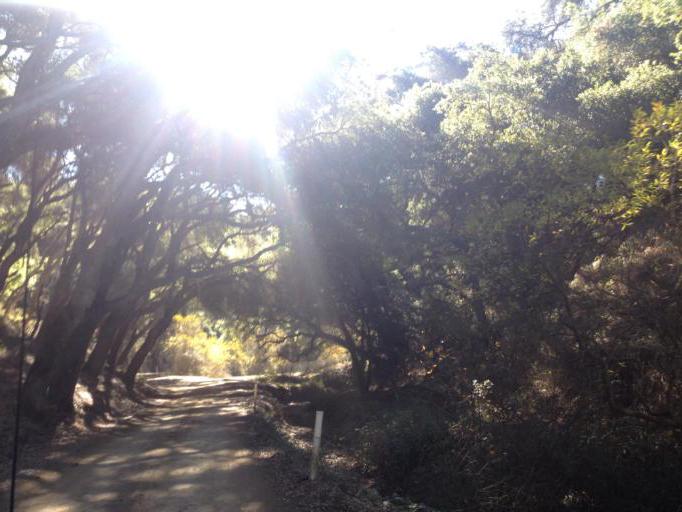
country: US
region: California
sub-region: San Luis Obispo County
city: Avila Beach
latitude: 35.2435
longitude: -120.7774
